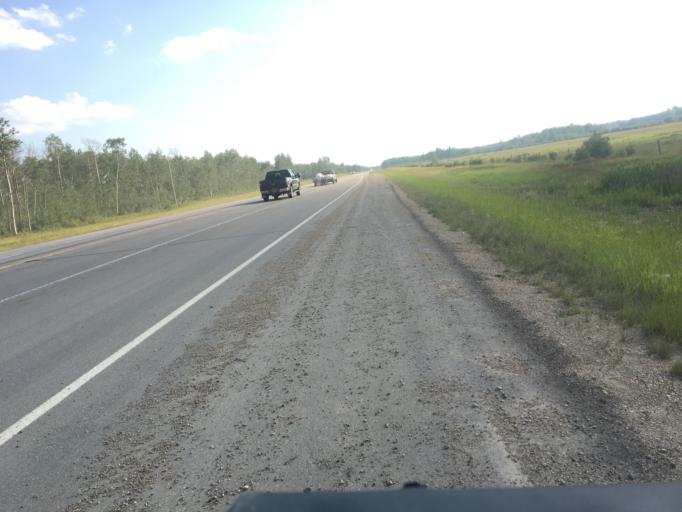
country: CA
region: Alberta
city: Sexsmith
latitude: 55.4316
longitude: -118.6929
